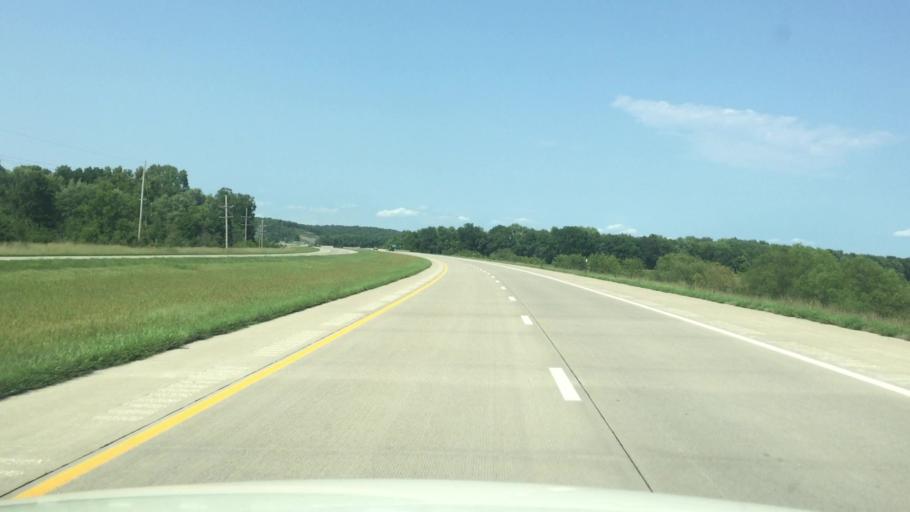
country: US
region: Kansas
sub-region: Linn County
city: Pleasanton
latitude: 38.2317
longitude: -94.6928
